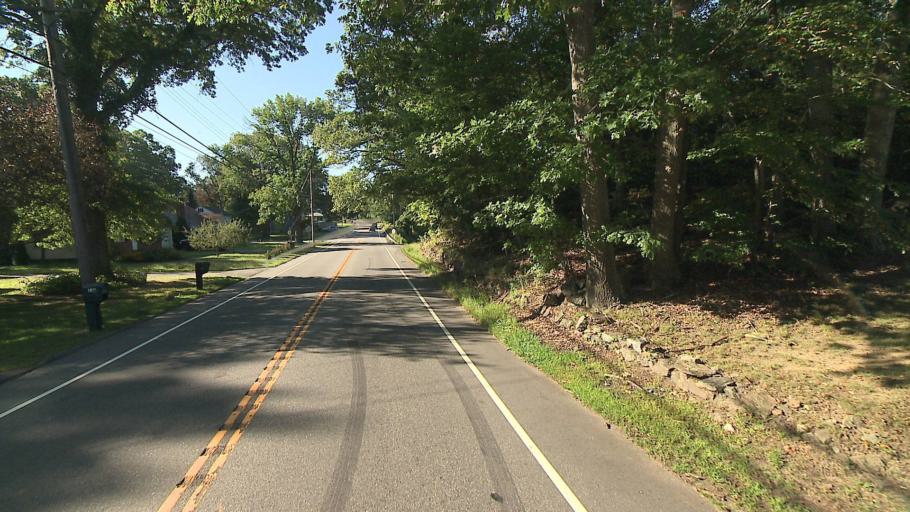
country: US
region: Connecticut
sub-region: New London County
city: Norwich
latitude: 41.5036
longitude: -72.0766
